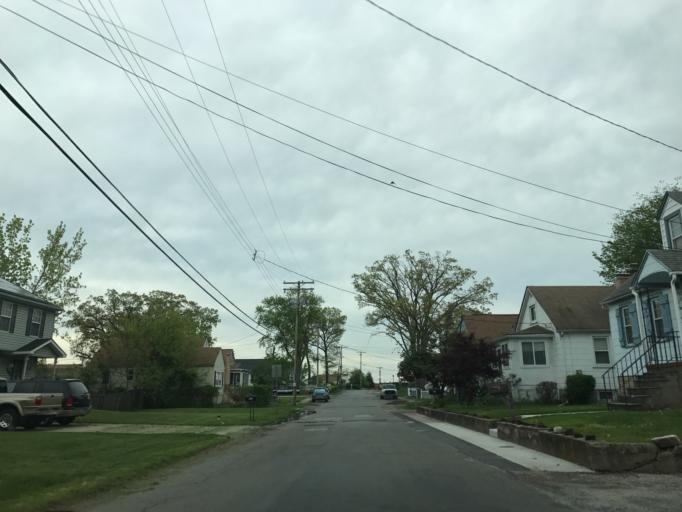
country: US
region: Maryland
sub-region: Baltimore County
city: Rosedale
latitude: 39.3190
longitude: -76.5080
